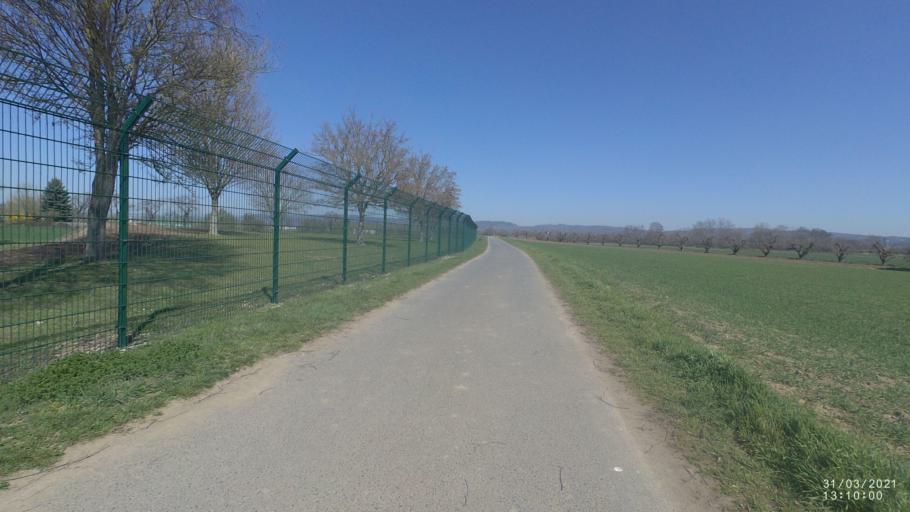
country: DE
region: Rheinland-Pfalz
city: Urmitz
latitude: 50.4075
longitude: 7.5323
